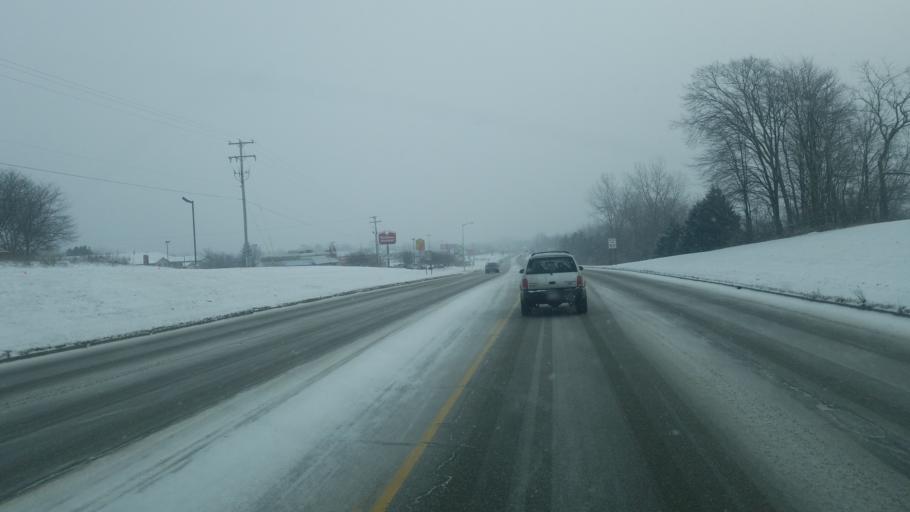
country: US
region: Michigan
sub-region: Mecosta County
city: Big Rapids
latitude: 43.6875
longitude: -85.4979
